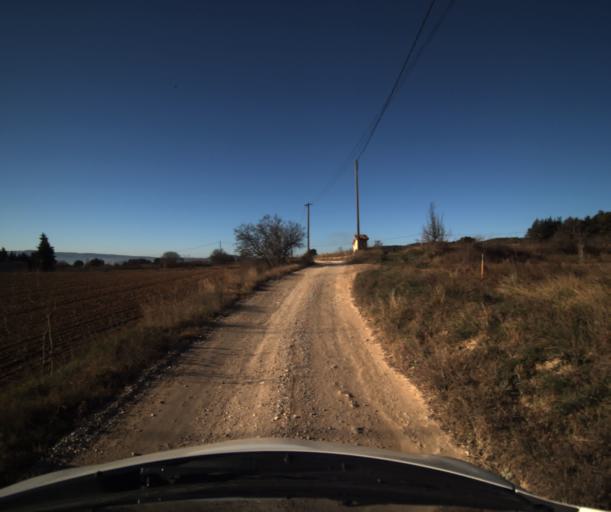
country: FR
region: Provence-Alpes-Cote d'Azur
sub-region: Departement du Vaucluse
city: Pertuis
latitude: 43.7118
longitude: 5.5032
